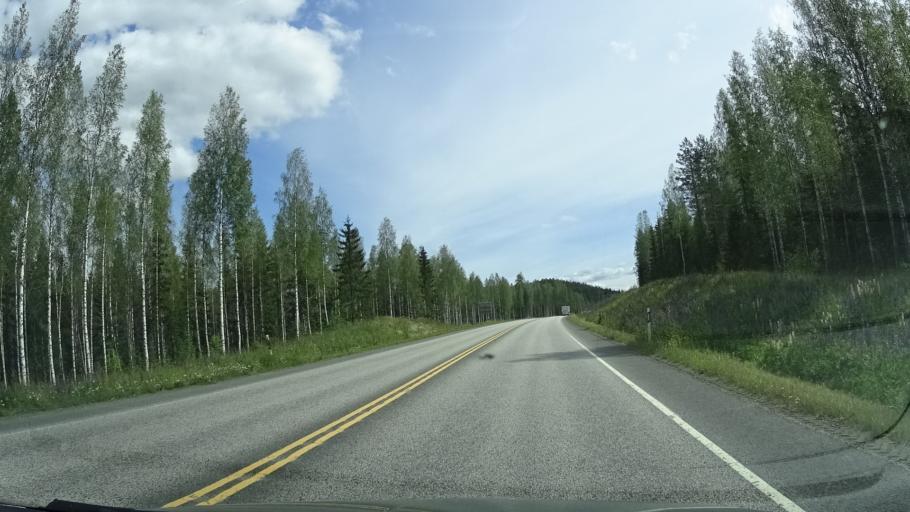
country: FI
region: Central Finland
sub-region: Jyvaeskylae
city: Jyvaeskylae
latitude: 62.2532
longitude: 25.6350
